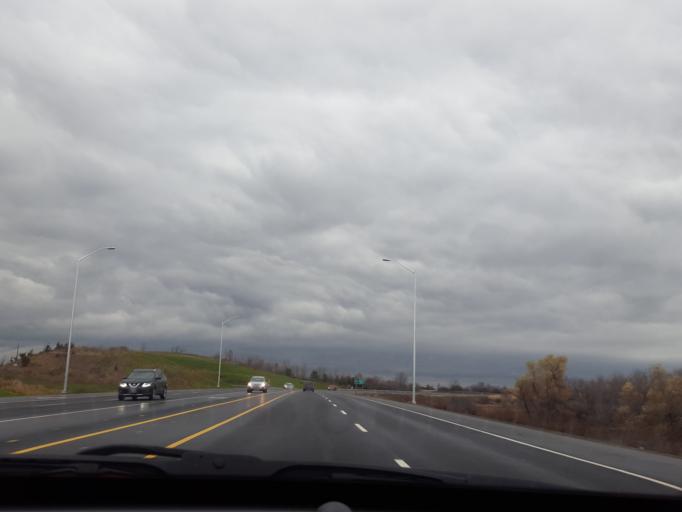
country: CA
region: Ontario
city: Pickering
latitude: 43.9024
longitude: -79.0971
